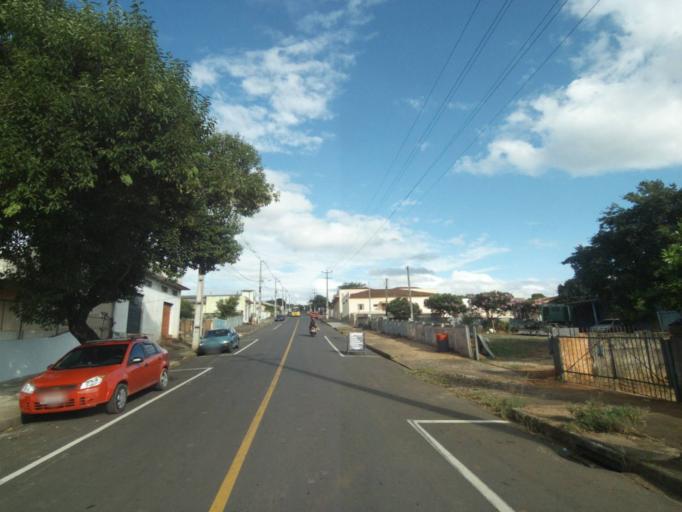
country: BR
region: Parana
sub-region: Telemaco Borba
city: Telemaco Borba
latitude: -24.3377
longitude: -50.6154
